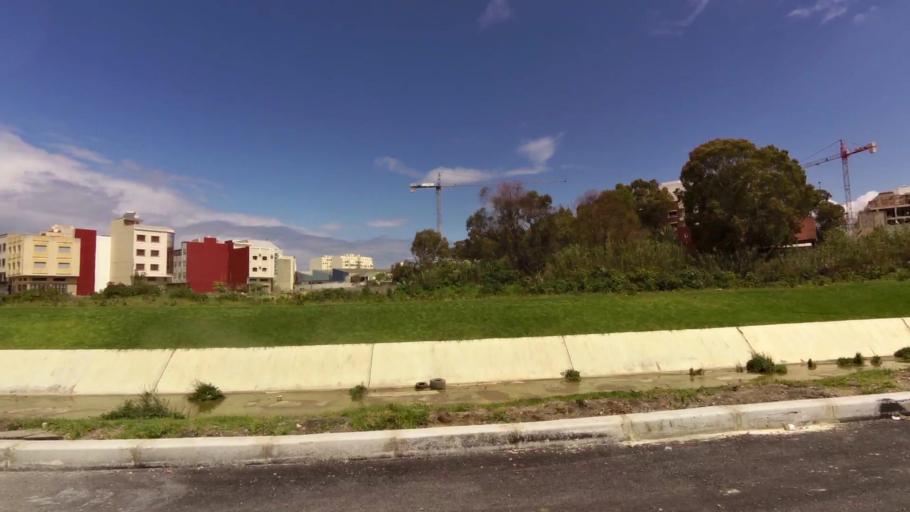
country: MA
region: Tanger-Tetouan
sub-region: Tanger-Assilah
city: Tangier
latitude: 35.7614
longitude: -5.8452
